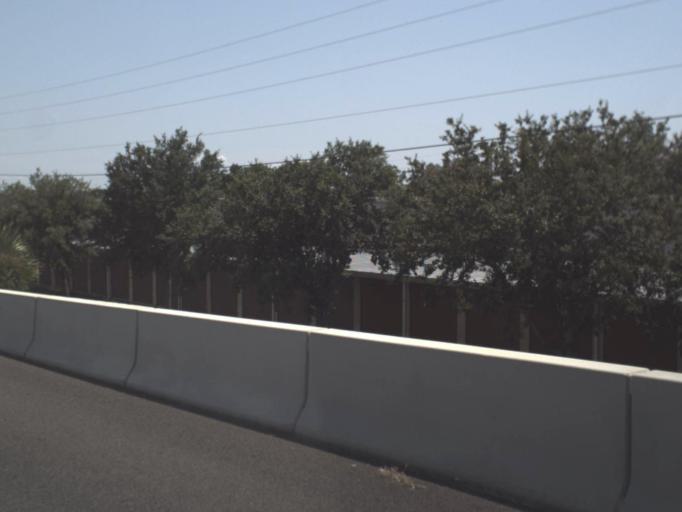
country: US
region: Florida
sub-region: Pinellas County
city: Pinellas Park
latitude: 27.8698
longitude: -82.7056
